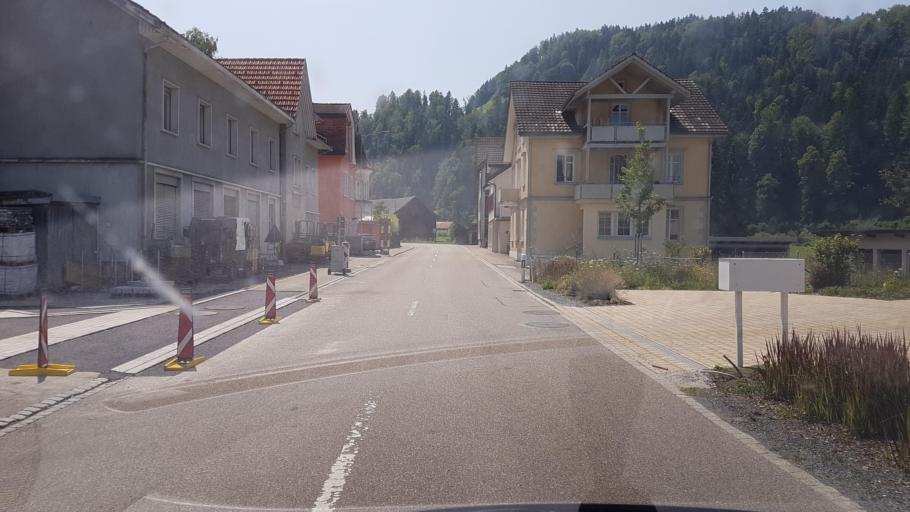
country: CH
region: Saint Gallen
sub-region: Wahlkreis Toggenburg
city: Mogelsberg
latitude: 47.3460
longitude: 9.1303
